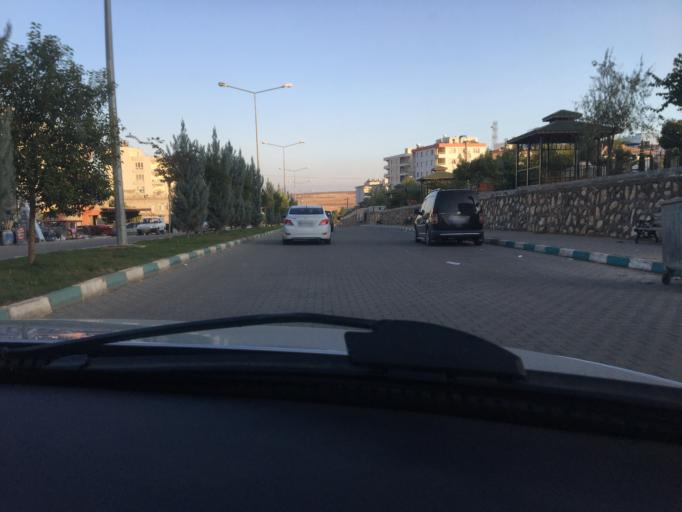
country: TR
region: Sanliurfa
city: Halfeti
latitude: 37.2306
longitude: 37.9468
